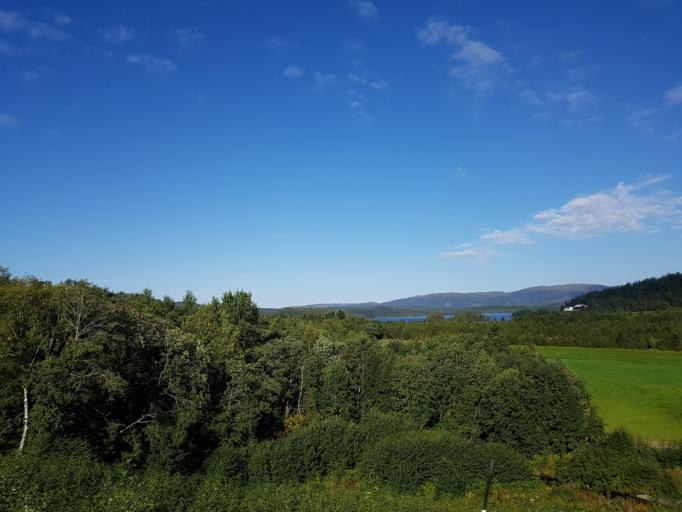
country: NO
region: Sor-Trondelag
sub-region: Trondheim
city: Trondheim
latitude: 63.6007
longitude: 10.2231
